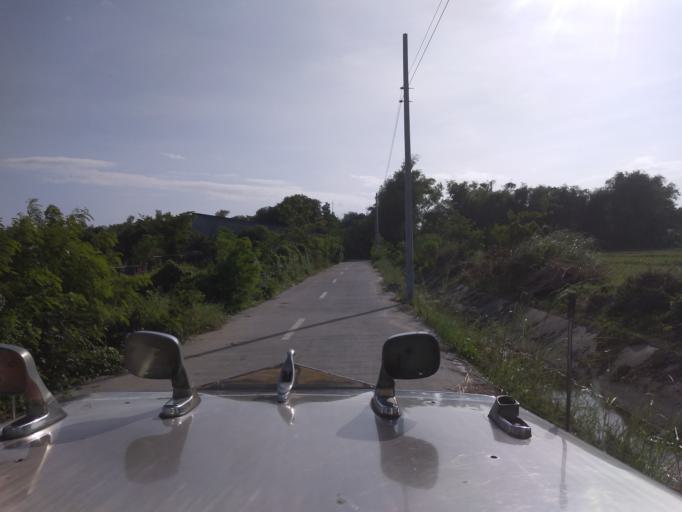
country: PH
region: Central Luzon
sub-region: Province of Pampanga
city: San Patricio
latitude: 15.0941
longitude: 120.6969
